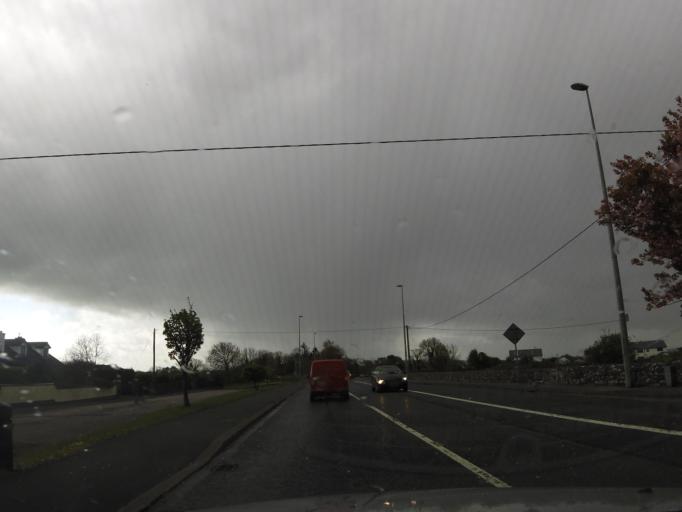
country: IE
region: Connaught
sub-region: County Galway
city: Claregalway
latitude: 53.3310
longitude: -8.9625
